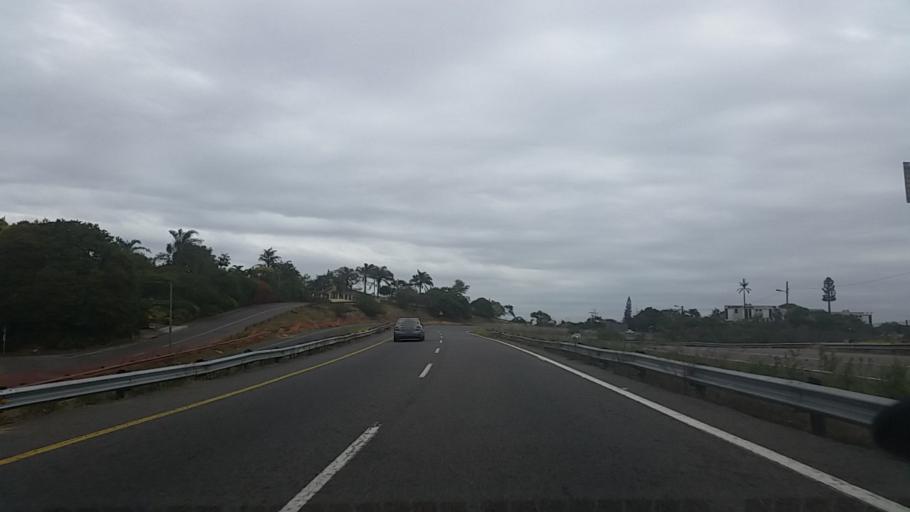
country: ZA
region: KwaZulu-Natal
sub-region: eThekwini Metropolitan Municipality
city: Berea
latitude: -29.8294
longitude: 30.9564
